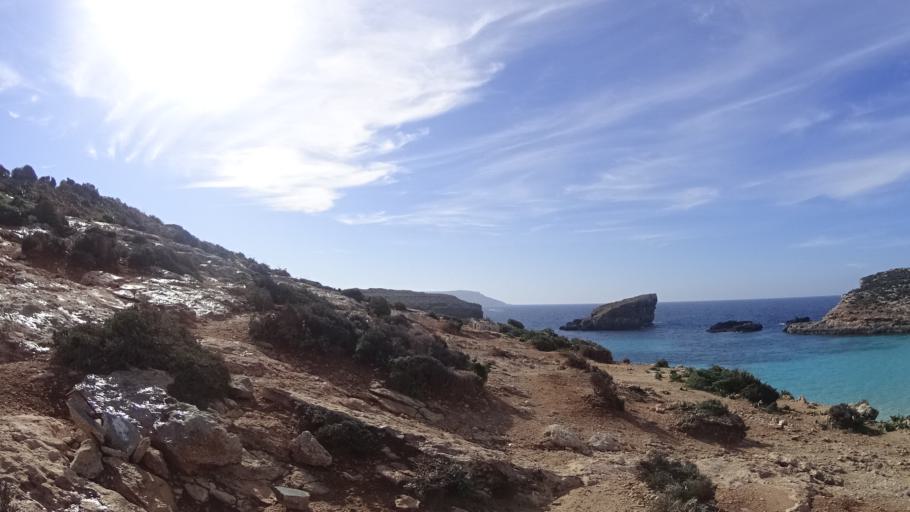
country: MT
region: Il-Qala
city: Qala
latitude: 36.0136
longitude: 14.3242
